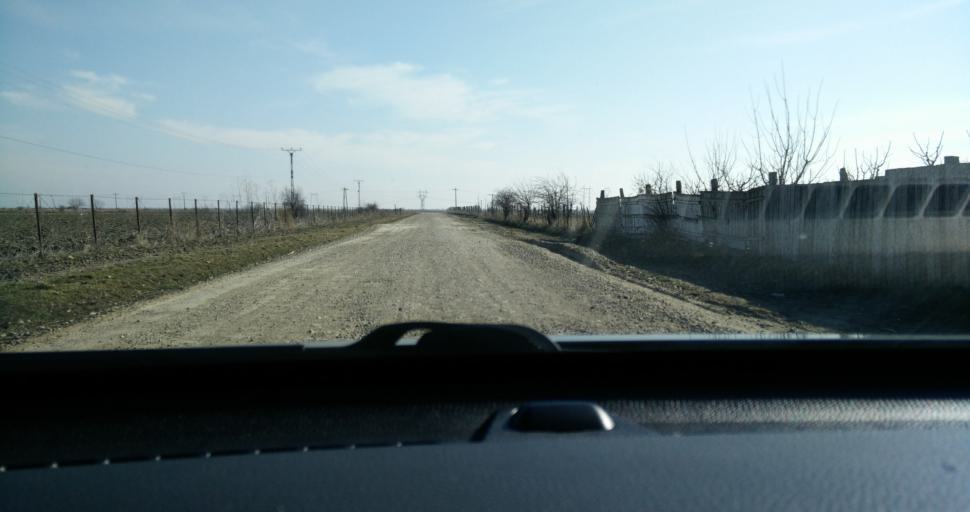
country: RO
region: Vrancea
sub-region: Comuna Suraia
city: Suraia
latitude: 45.6617
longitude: 27.3961
